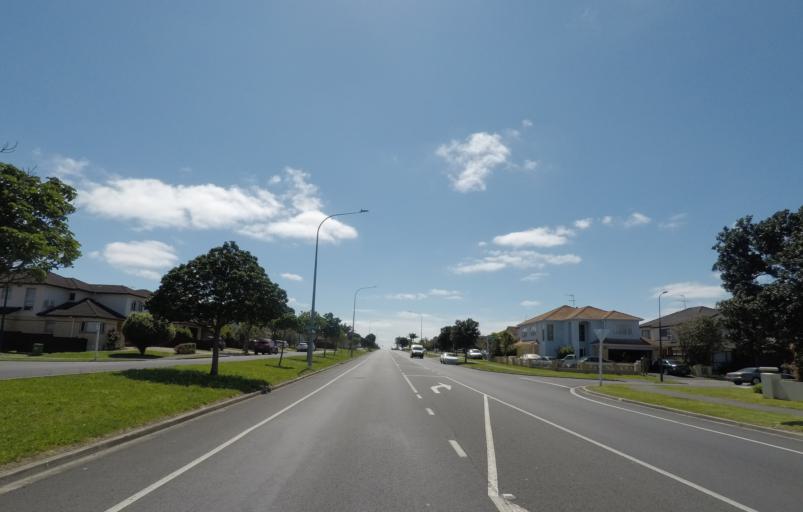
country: NZ
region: Auckland
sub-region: Auckland
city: Manukau City
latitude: -36.9524
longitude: 174.9100
